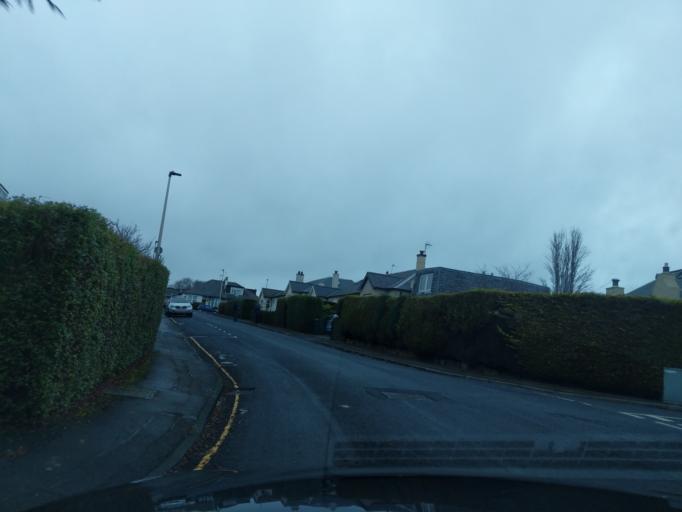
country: GB
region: Scotland
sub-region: Edinburgh
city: Edinburgh
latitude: 55.9558
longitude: -3.2335
